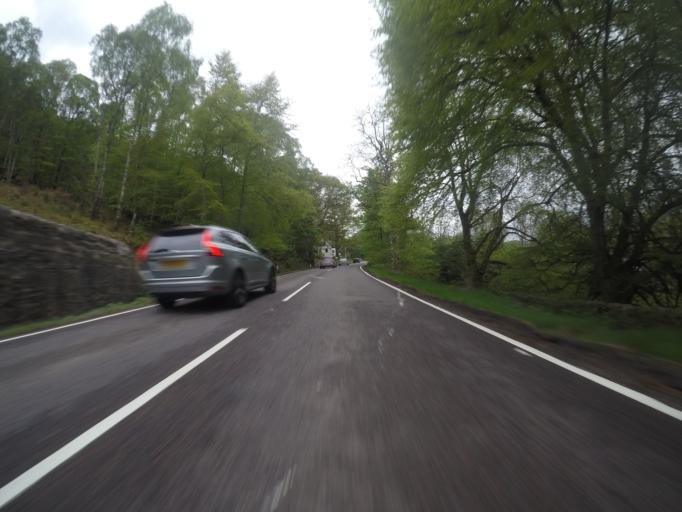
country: GB
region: Scotland
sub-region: Highland
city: Beauly
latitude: 57.2133
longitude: -4.6001
